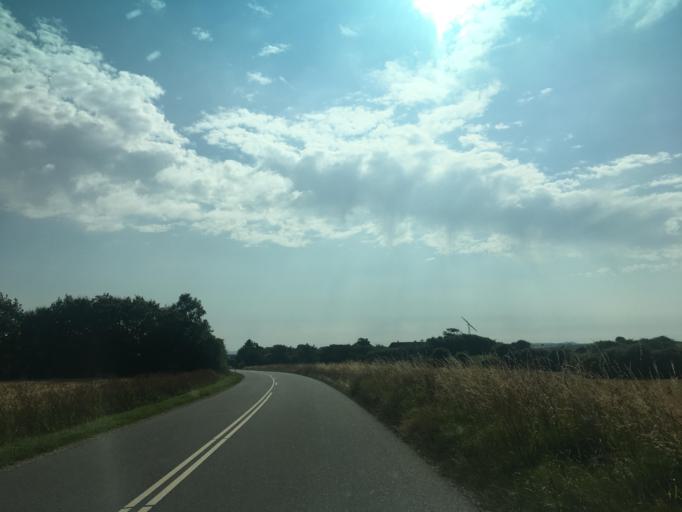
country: DK
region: North Denmark
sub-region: Thisted Kommune
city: Hurup
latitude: 56.8340
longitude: 8.5692
